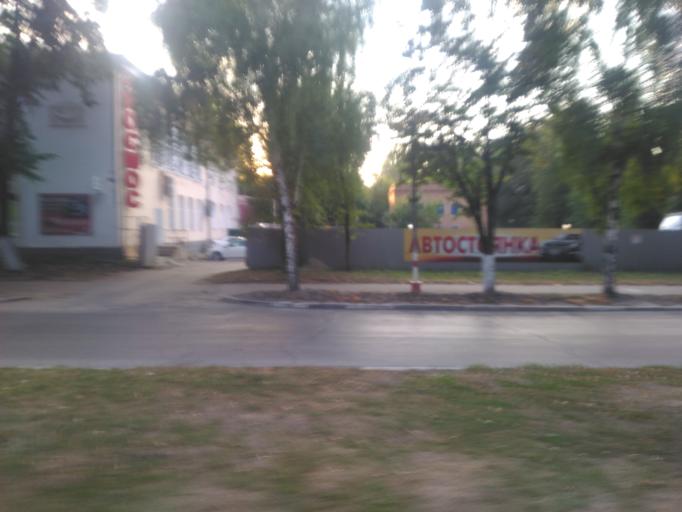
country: RU
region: Ulyanovsk
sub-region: Ulyanovskiy Rayon
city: Ulyanovsk
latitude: 54.3057
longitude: 48.3231
